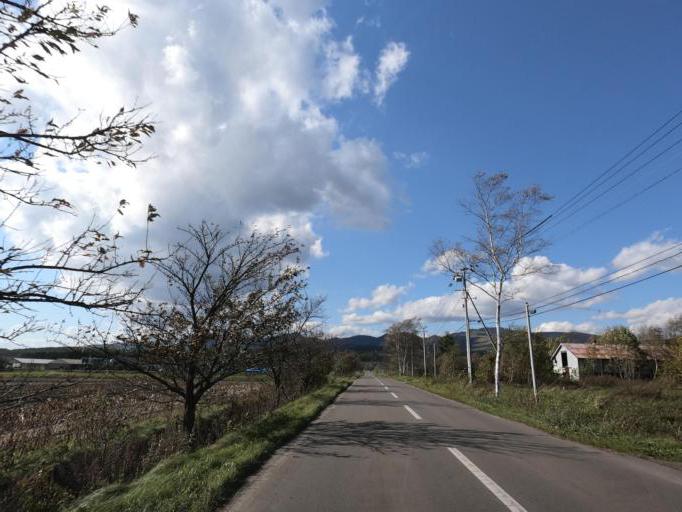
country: JP
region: Hokkaido
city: Otofuke
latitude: 43.2579
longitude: 143.2509
